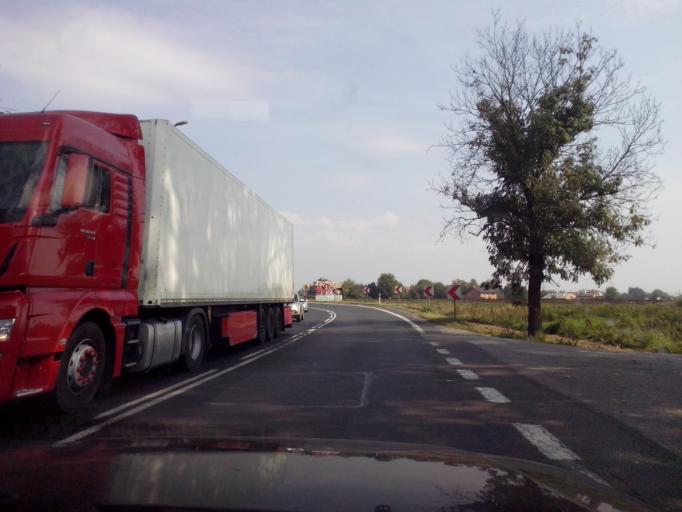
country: PL
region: Subcarpathian Voivodeship
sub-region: Powiat rzeszowski
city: Lutoryz
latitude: 49.9617
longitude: 21.9205
